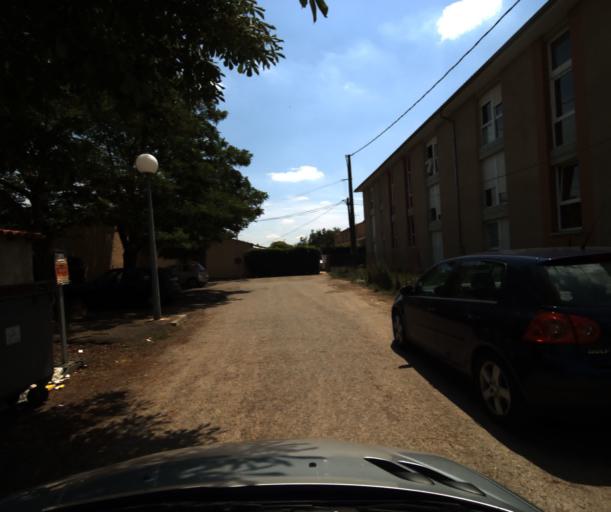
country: FR
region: Midi-Pyrenees
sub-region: Departement de la Haute-Garonne
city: Saint-Lys
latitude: 43.5087
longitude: 1.1721
